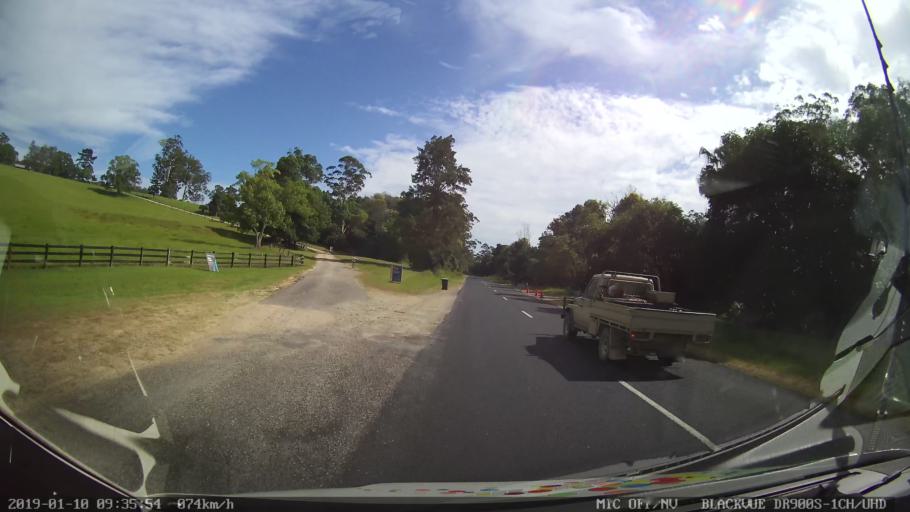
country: AU
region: New South Wales
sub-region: Coffs Harbour
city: Nana Glen
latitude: -30.2048
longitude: 153.0127
